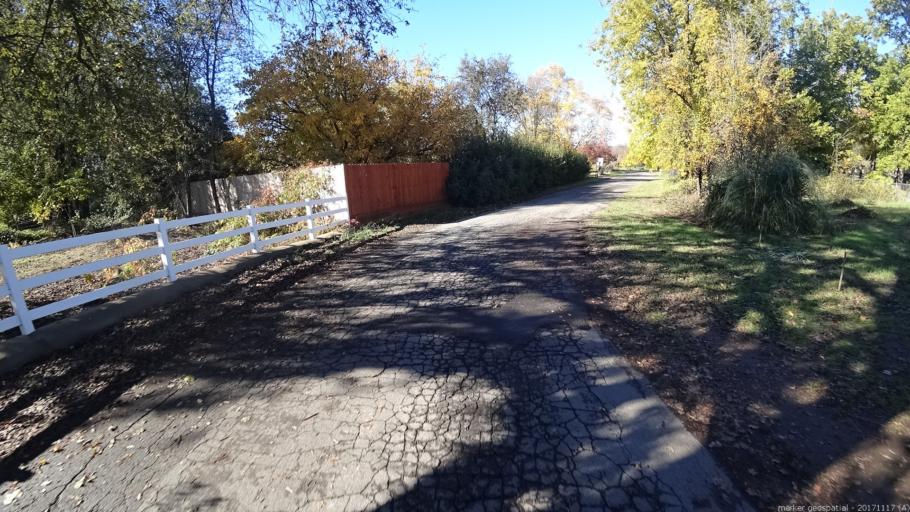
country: US
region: California
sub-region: Shasta County
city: Anderson
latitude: 40.4455
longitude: -122.2409
